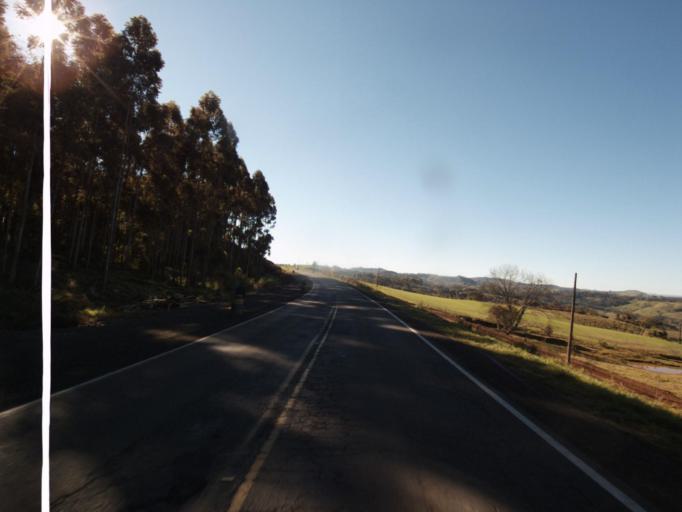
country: AR
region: Misiones
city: Bernardo de Irigoyen
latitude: -26.6249
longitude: -53.5159
